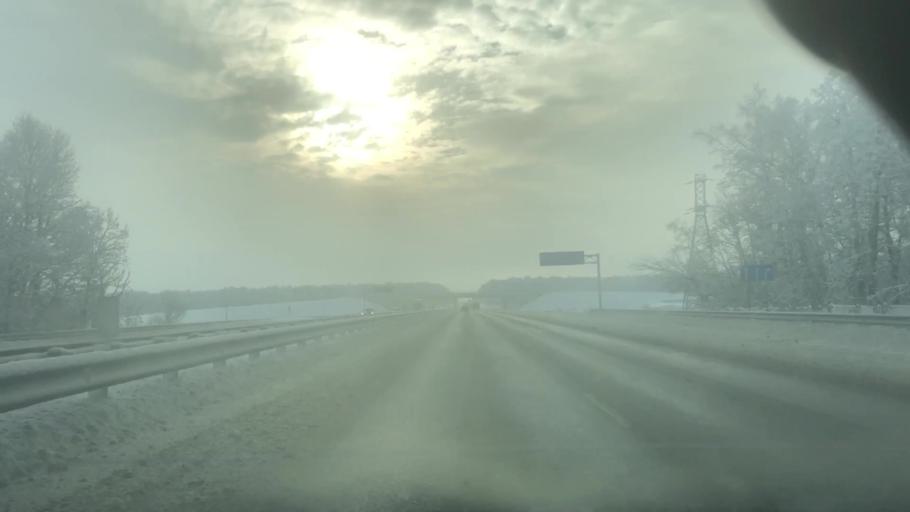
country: RU
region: Tula
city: Venev
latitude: 54.3782
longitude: 38.1549
